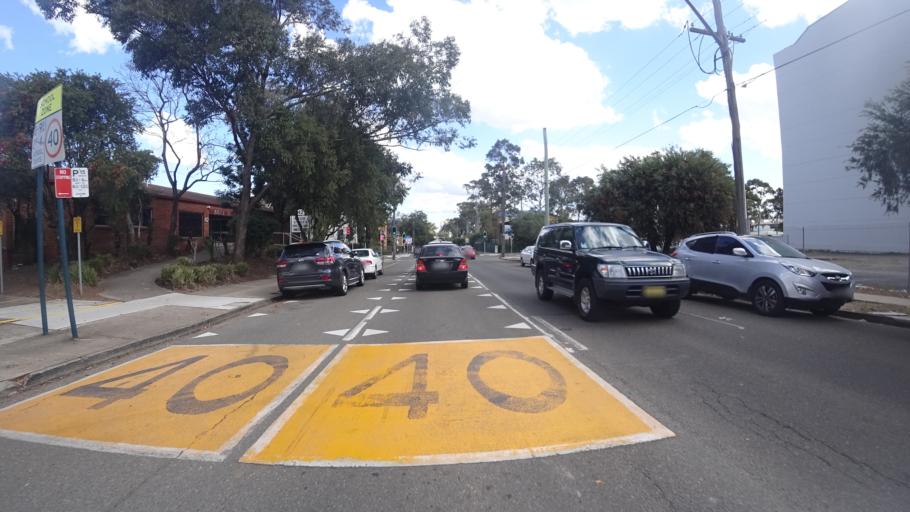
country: AU
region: New South Wales
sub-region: Fairfield
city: Liverpool
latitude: -33.9177
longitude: 150.9279
